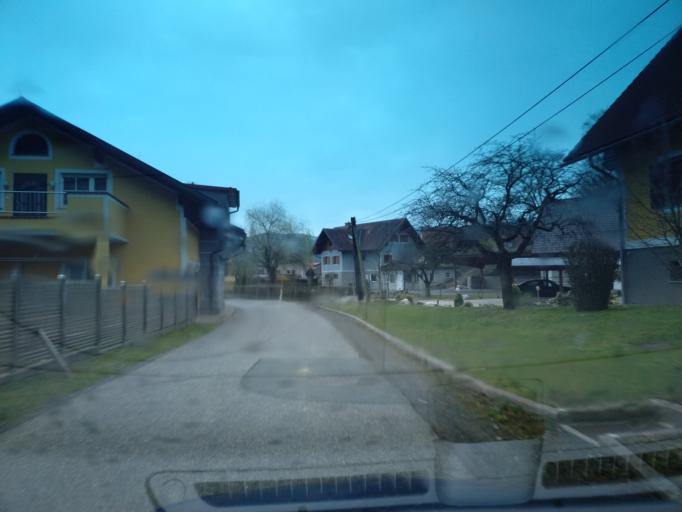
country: AT
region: Styria
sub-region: Politischer Bezirk Leibnitz
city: Oberhaag
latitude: 46.6972
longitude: 15.3666
